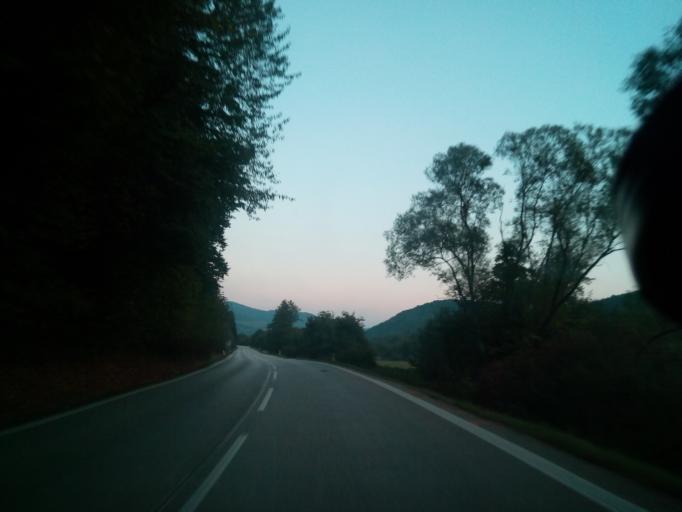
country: SK
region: Kosicky
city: Dobsina
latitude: 48.7872
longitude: 20.4019
